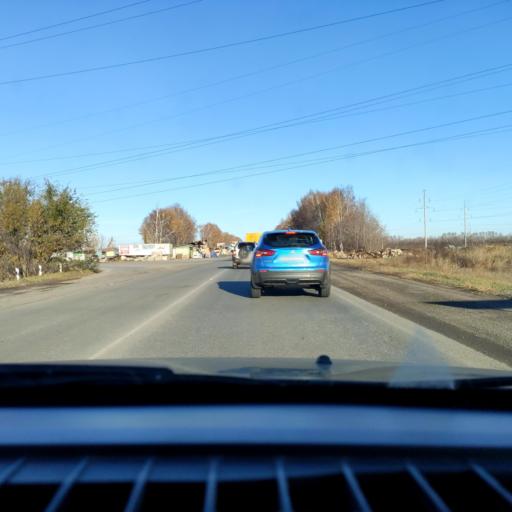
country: RU
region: Samara
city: Tol'yatti
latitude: 53.5874
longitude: 49.3313
